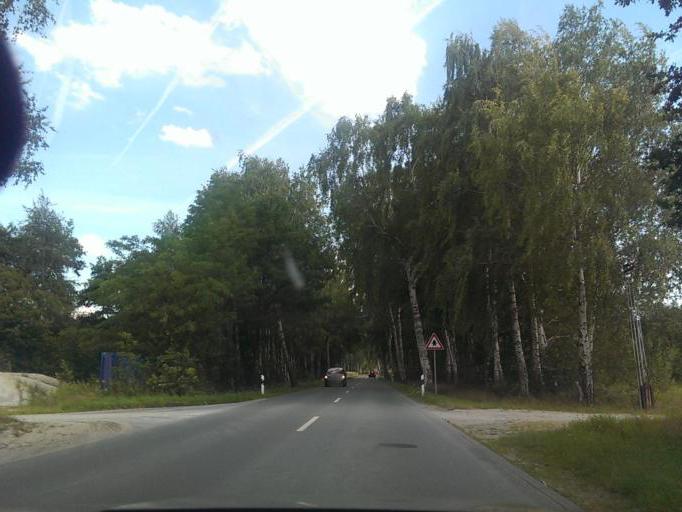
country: DE
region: North Rhine-Westphalia
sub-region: Regierungsbezirk Detmold
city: Delbruck
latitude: 51.7308
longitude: 8.5290
